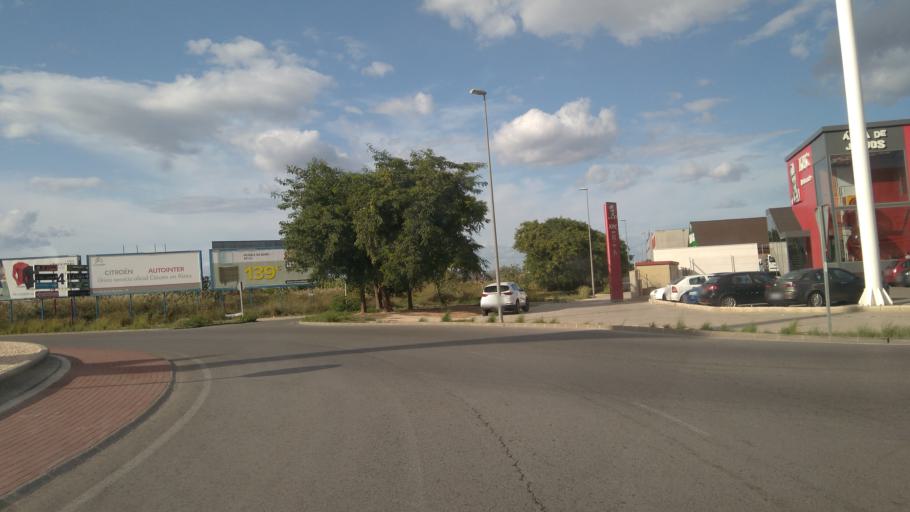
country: ES
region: Valencia
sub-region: Provincia de Valencia
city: Alzira
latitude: 39.1606
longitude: -0.4315
